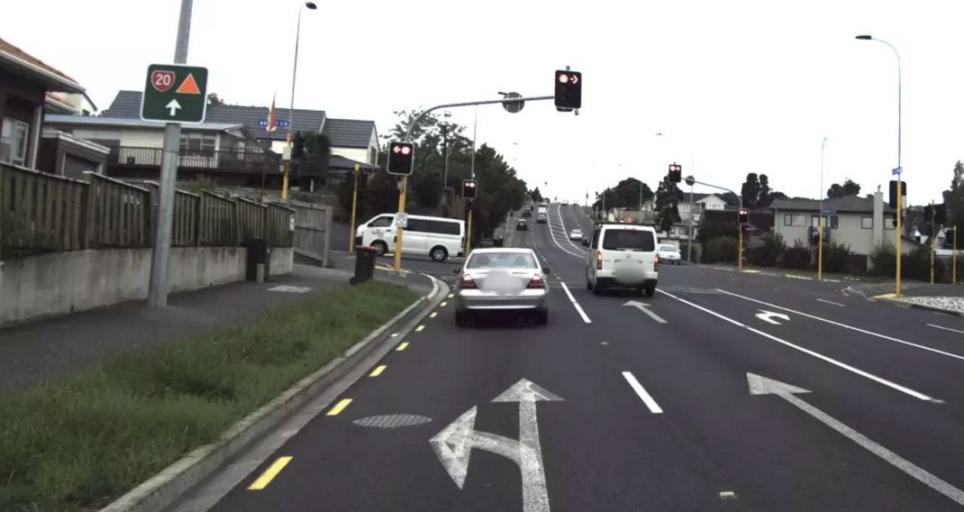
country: NZ
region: Auckland
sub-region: Auckland
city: Rosebank
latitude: -36.9056
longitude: 174.7074
